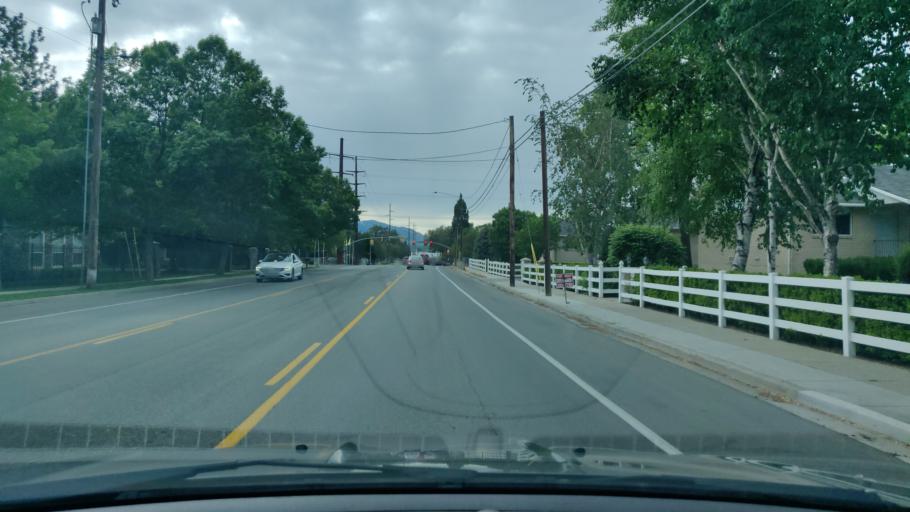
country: US
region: Utah
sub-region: Salt Lake County
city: Little Cottonwood Creek Valley
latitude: 40.6185
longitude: -111.8601
